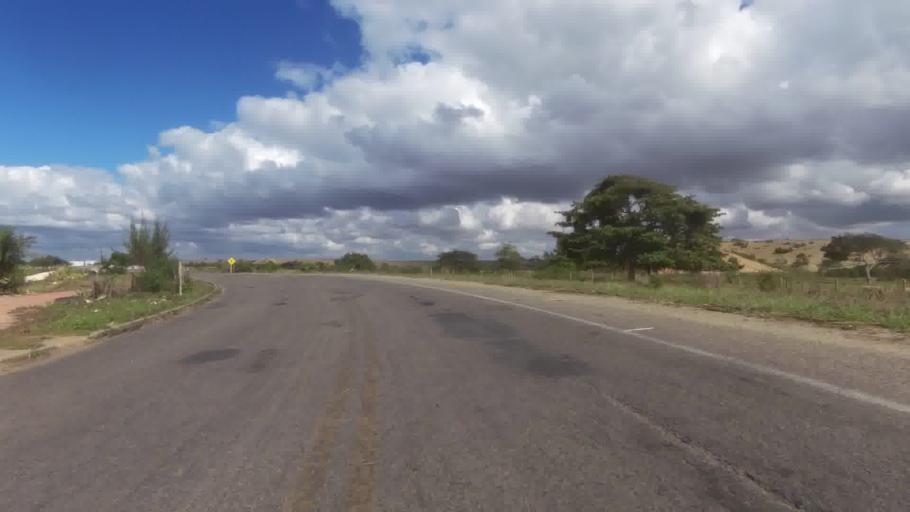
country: BR
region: Espirito Santo
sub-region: Marataizes
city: Marataizes
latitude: -21.1850
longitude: -40.9314
